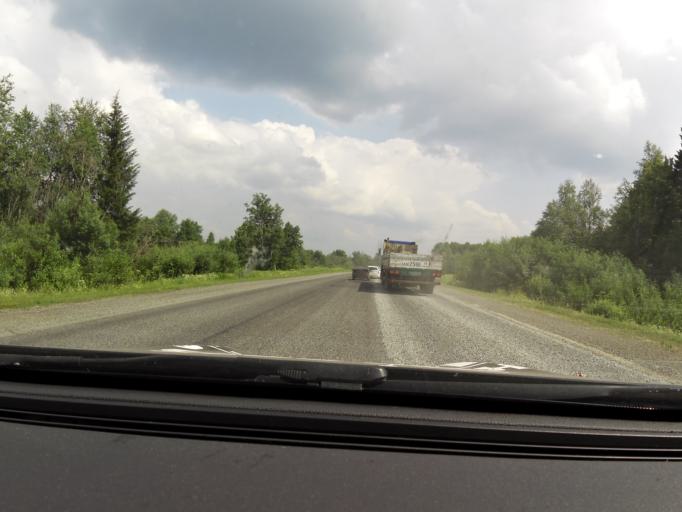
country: RU
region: Sverdlovsk
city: Ufimskiy
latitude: 56.7703
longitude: 58.1219
